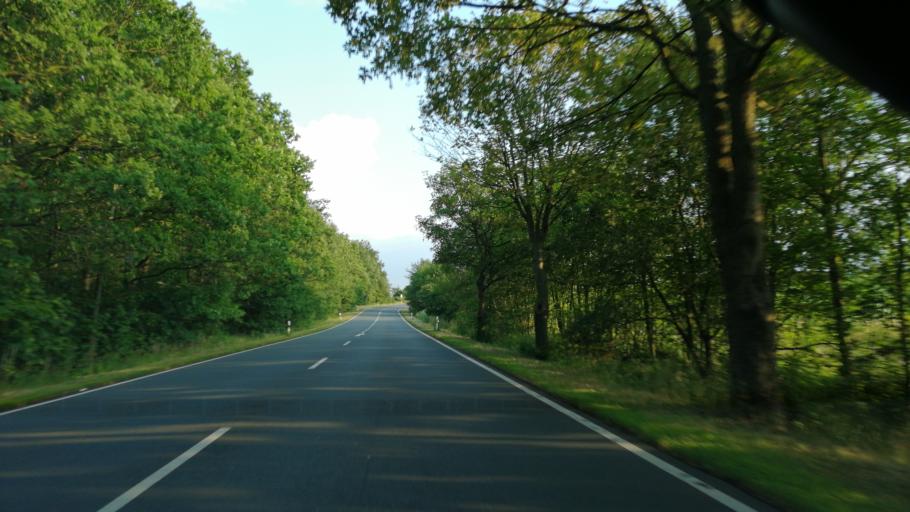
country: DE
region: Saxony-Anhalt
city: Riestedt
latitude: 51.5219
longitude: 11.3798
